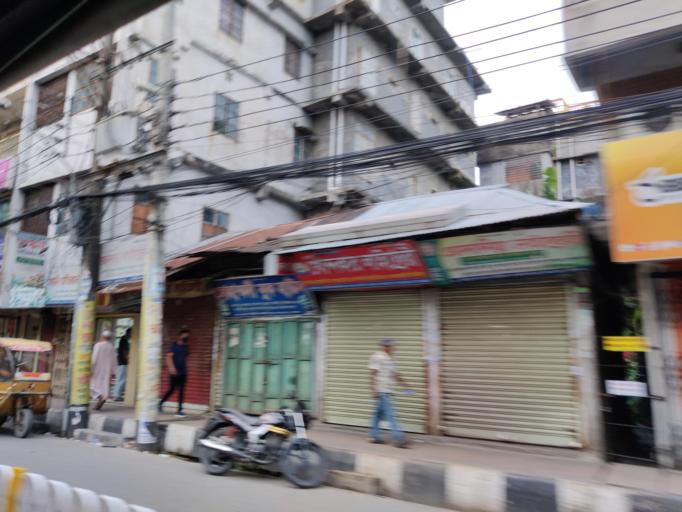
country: BD
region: Barisal
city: Barisal
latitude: 22.7060
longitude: 90.3708
